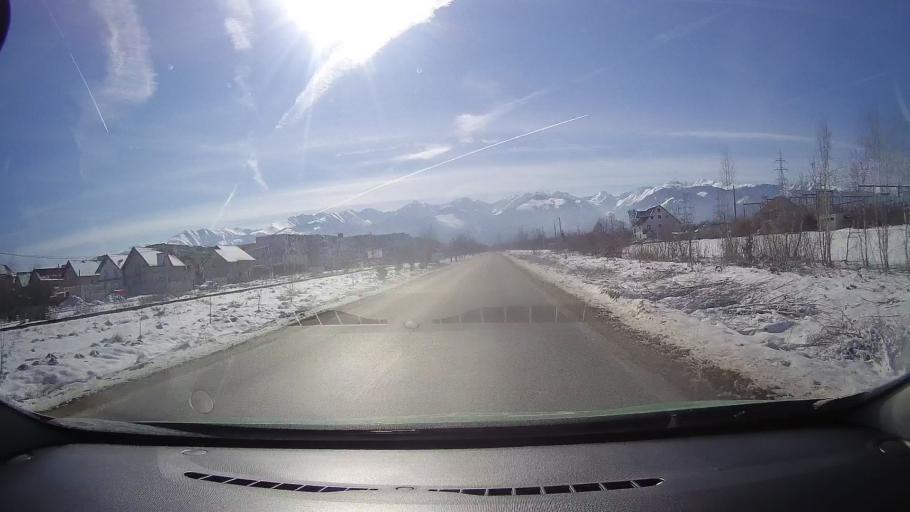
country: RO
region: Brasov
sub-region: Oras Victoria
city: Victoria
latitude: 45.7354
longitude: 24.6950
